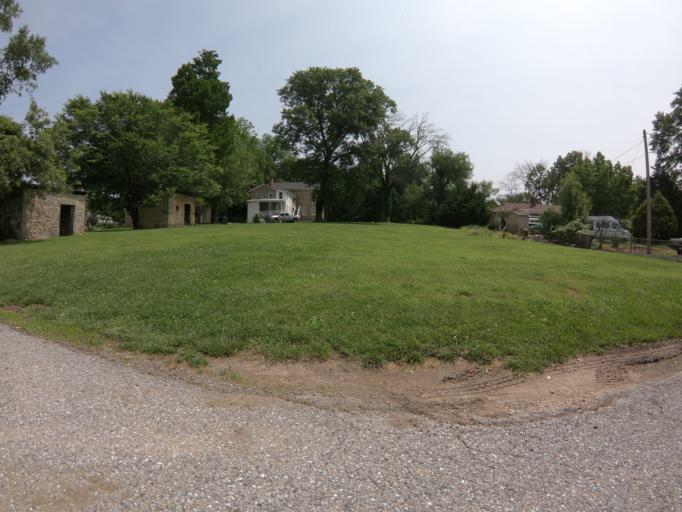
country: US
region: Maryland
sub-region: Howard County
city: Ellicott City
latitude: 39.2377
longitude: -76.8032
